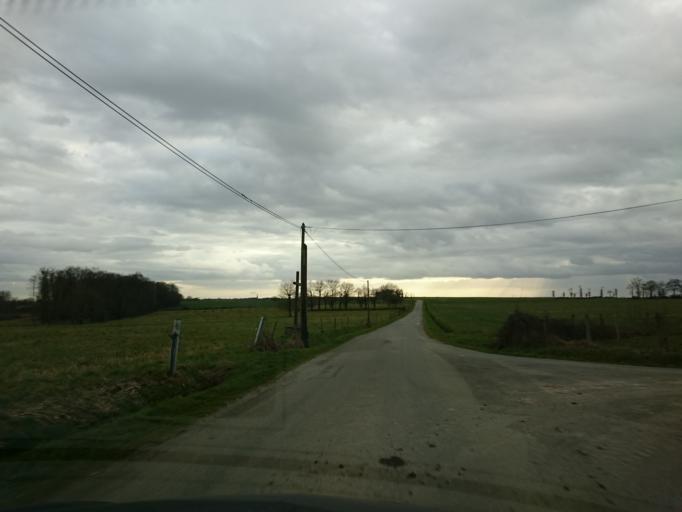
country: FR
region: Brittany
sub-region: Departement d'Ille-et-Vilaine
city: Pance
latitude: 47.9080
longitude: -1.6419
